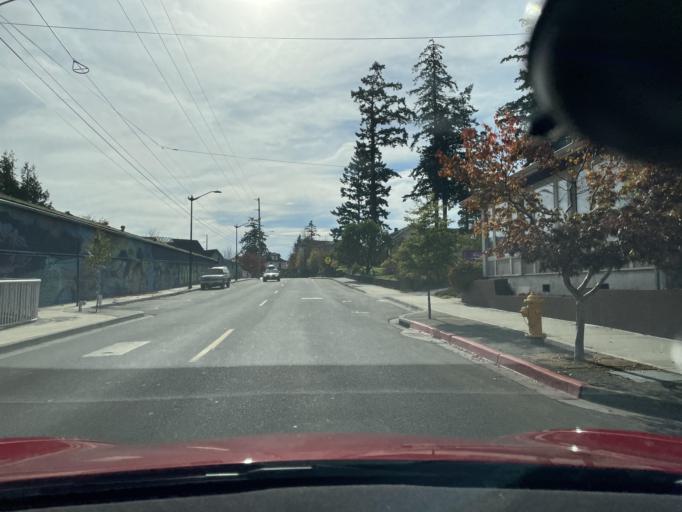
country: US
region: Washington
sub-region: San Juan County
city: Friday Harbor
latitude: 48.5336
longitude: -123.0204
